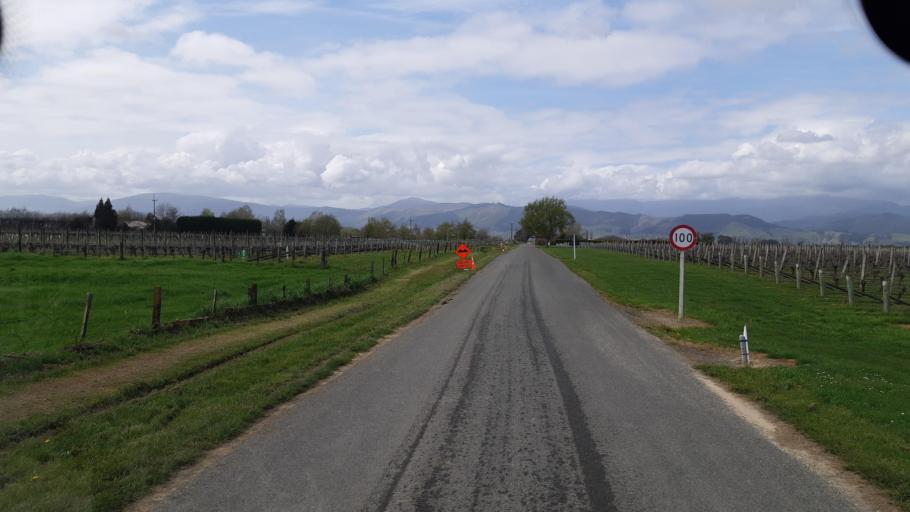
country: NZ
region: Tasman
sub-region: Tasman District
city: Brightwater
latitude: -41.3292
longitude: 173.1024
